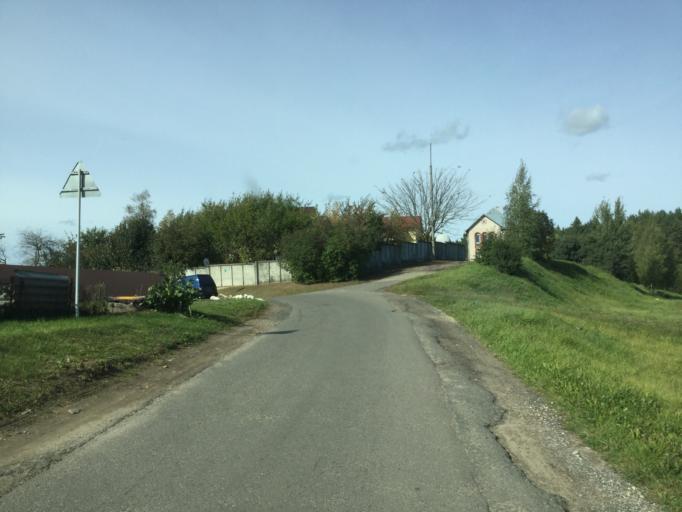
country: BY
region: Vitebsk
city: Orsha
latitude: 54.5477
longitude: 30.4443
